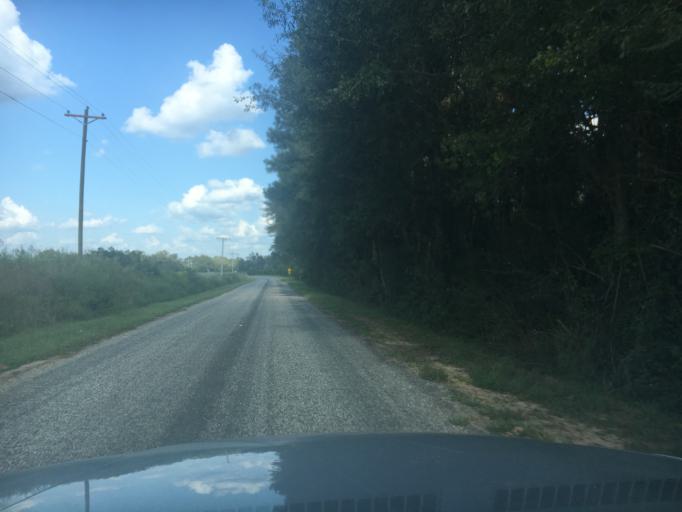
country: US
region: South Carolina
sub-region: Greenwood County
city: Ware Shoals
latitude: 34.4866
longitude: -82.2339
